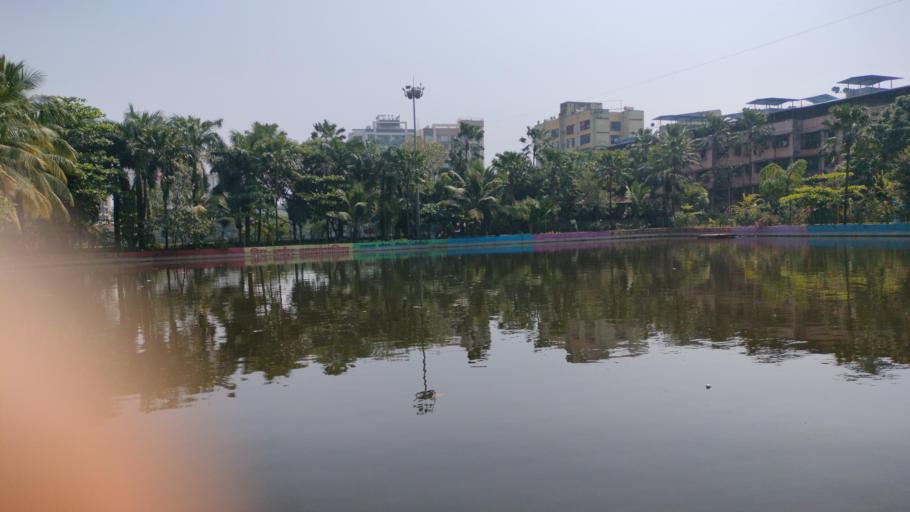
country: IN
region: Maharashtra
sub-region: Thane
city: Bhayandar
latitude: 19.3055
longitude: 72.8635
